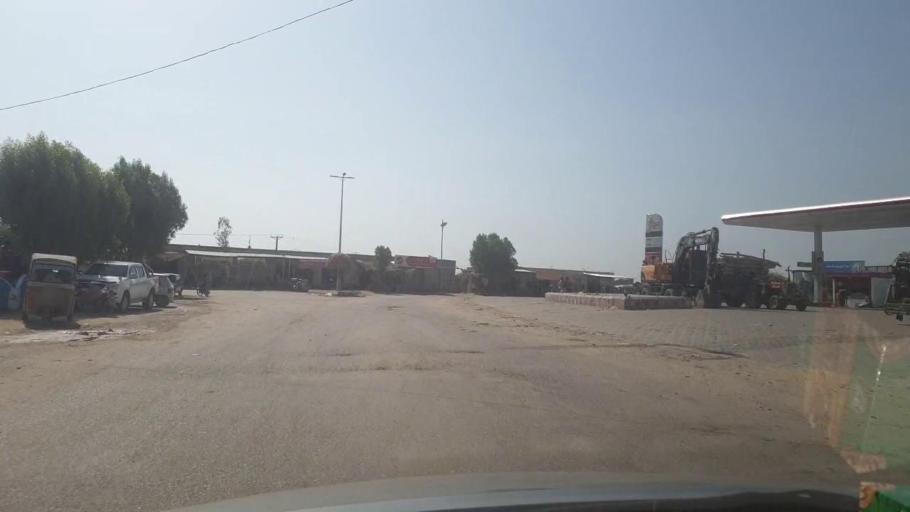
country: PK
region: Sindh
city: Rohri
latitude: 27.5037
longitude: 69.0398
